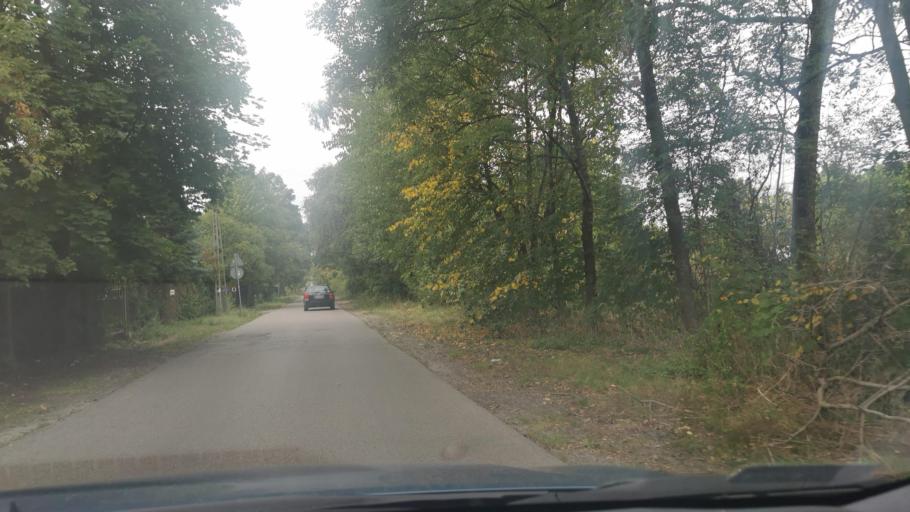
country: PL
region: Masovian Voivodeship
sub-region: Warszawa
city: Rembertow
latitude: 52.2303
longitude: 21.1422
